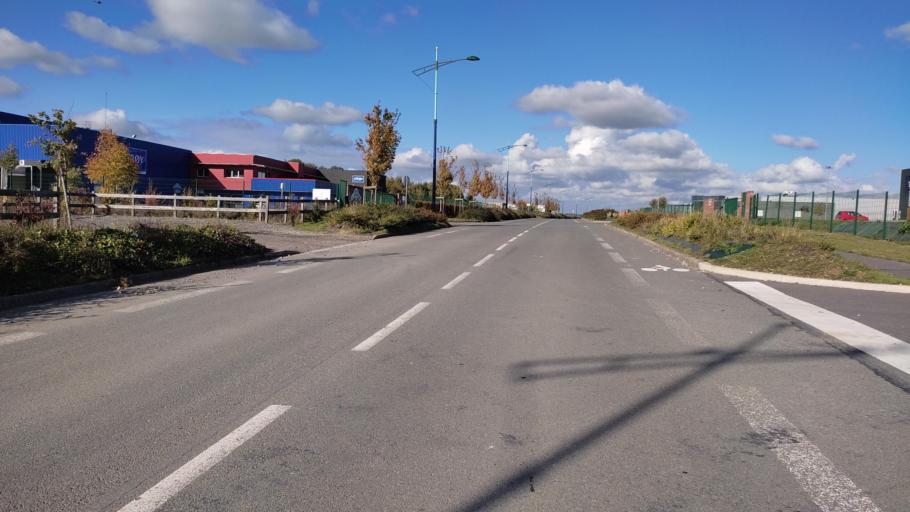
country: FR
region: Nord-Pas-de-Calais
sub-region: Departement du Pas-de-Calais
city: Saint-Laurent-Blangy
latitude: 50.3154
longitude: 2.8221
